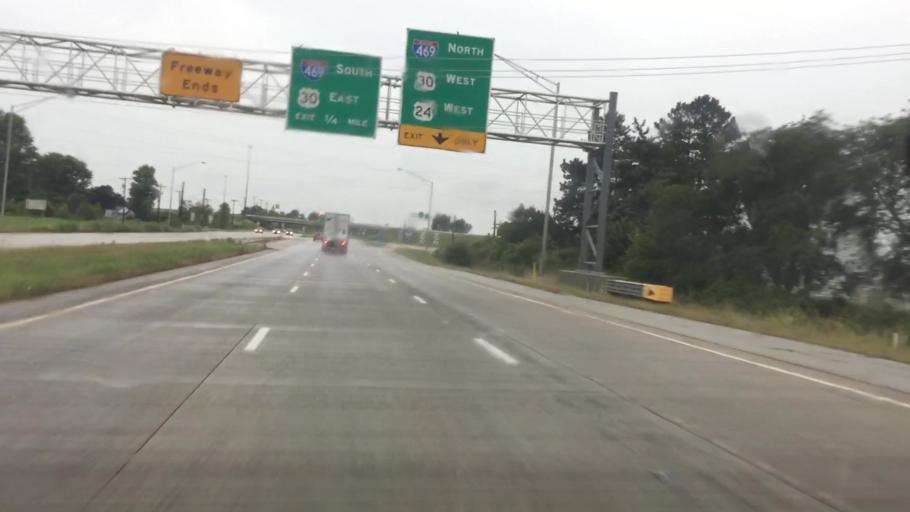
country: US
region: Indiana
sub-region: Allen County
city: New Haven
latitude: 41.0951
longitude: -84.9757
